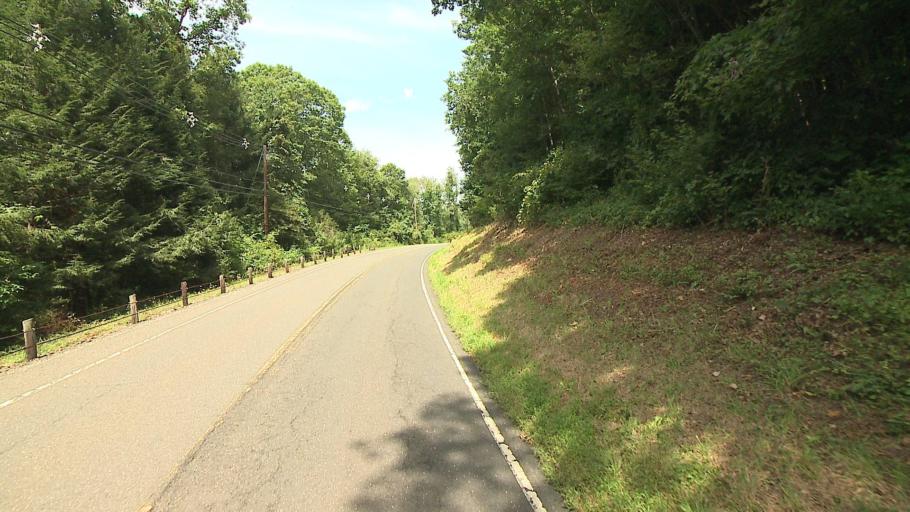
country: US
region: Connecticut
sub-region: Litchfield County
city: Bethlehem Village
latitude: 41.6329
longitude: -73.2224
